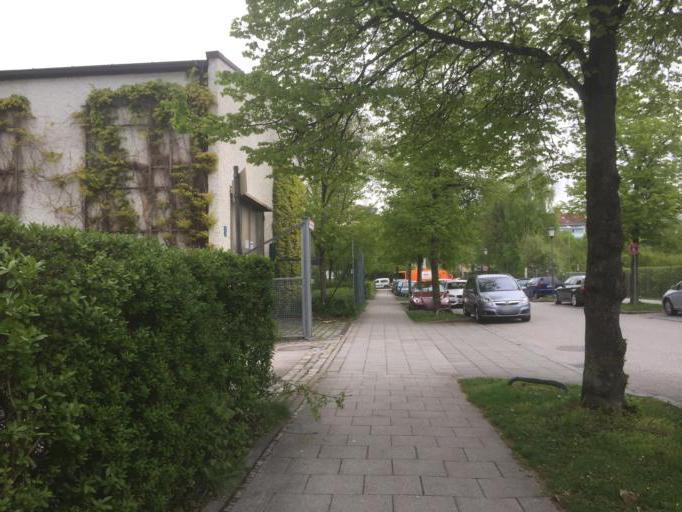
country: DE
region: Bavaria
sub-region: Upper Bavaria
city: Unterfoehring
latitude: 48.2013
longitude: 11.6028
